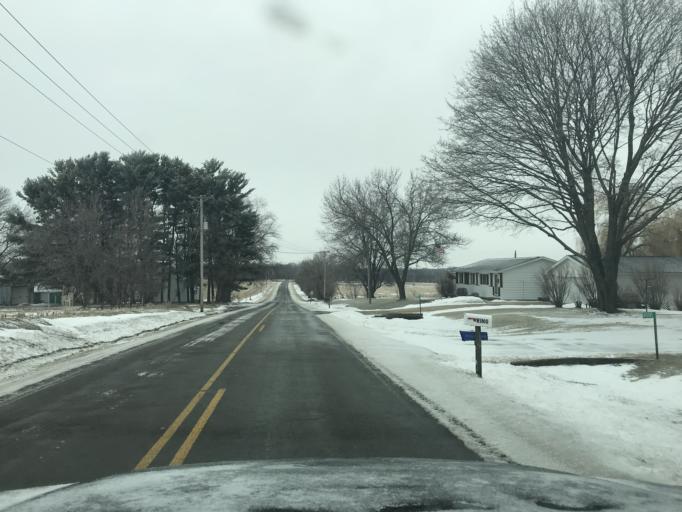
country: US
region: Wisconsin
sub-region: Dane County
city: Cottage Grove
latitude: 43.0946
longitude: -89.2296
